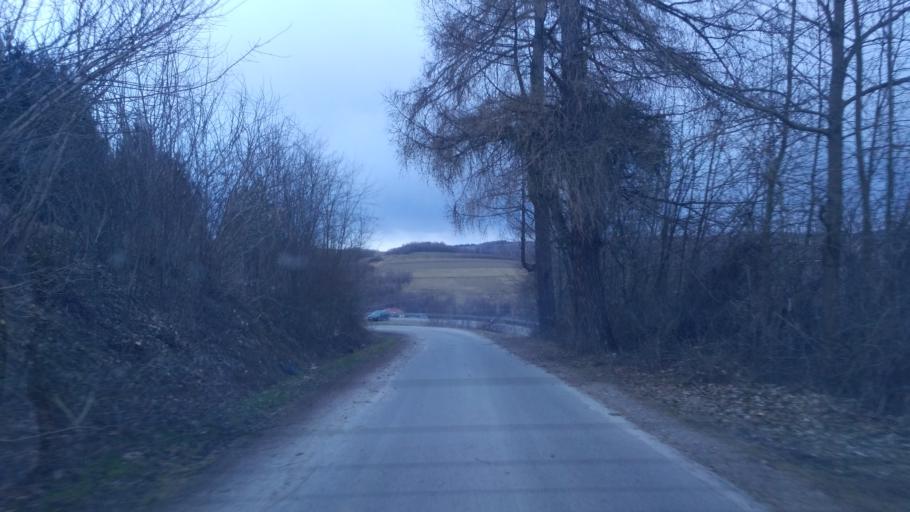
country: PL
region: Subcarpathian Voivodeship
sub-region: Powiat rzeszowski
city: Blazowa
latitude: 49.8882
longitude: 22.1076
